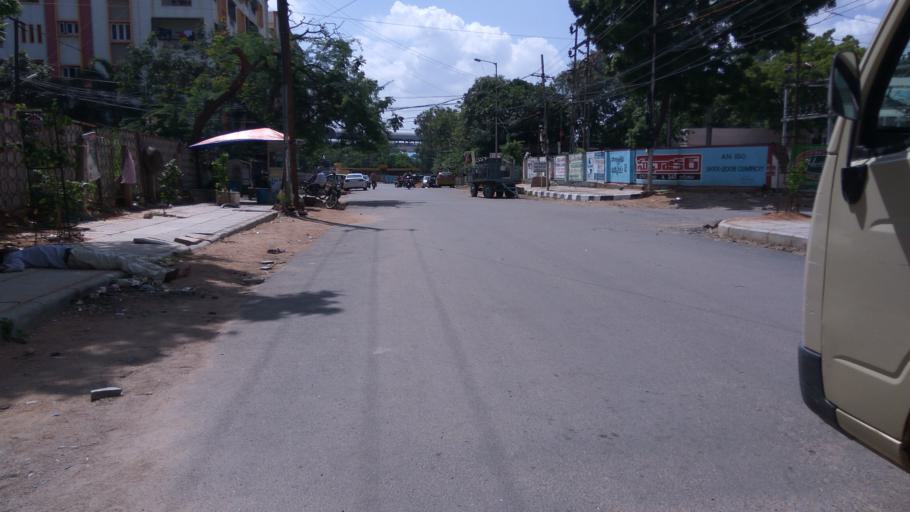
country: IN
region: Telangana
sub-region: Rangareddi
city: Kukatpalli
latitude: 17.4564
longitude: 78.4366
